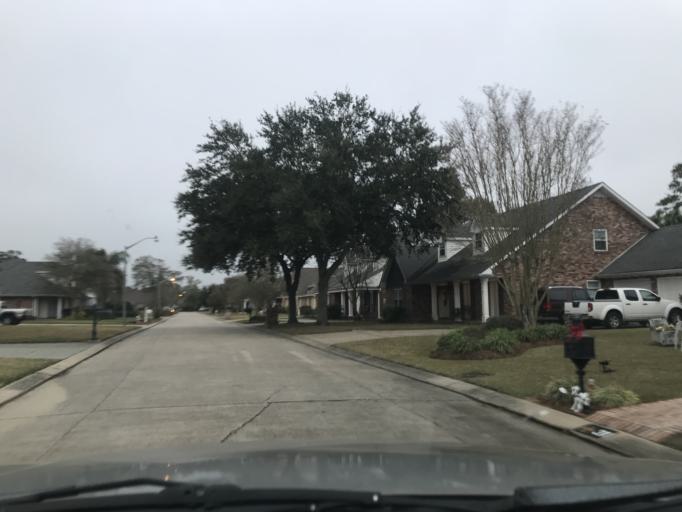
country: US
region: Louisiana
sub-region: Jefferson Parish
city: Woodmere
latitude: 29.8694
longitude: -90.0924
